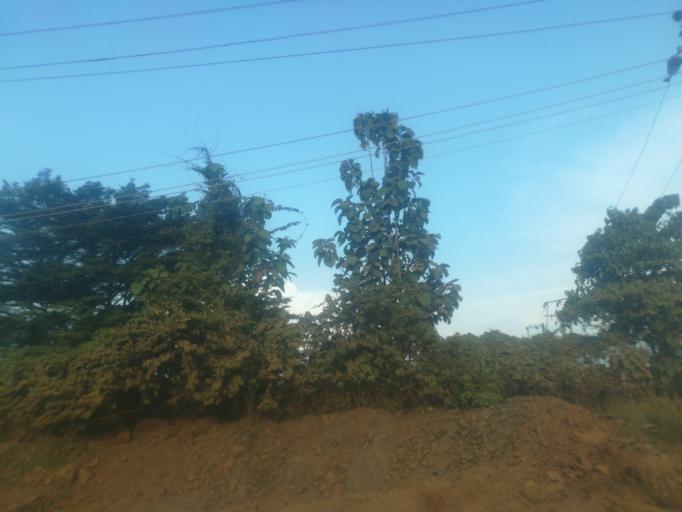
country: NG
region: Oyo
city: Moniya
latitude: 7.5393
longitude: 3.9001
